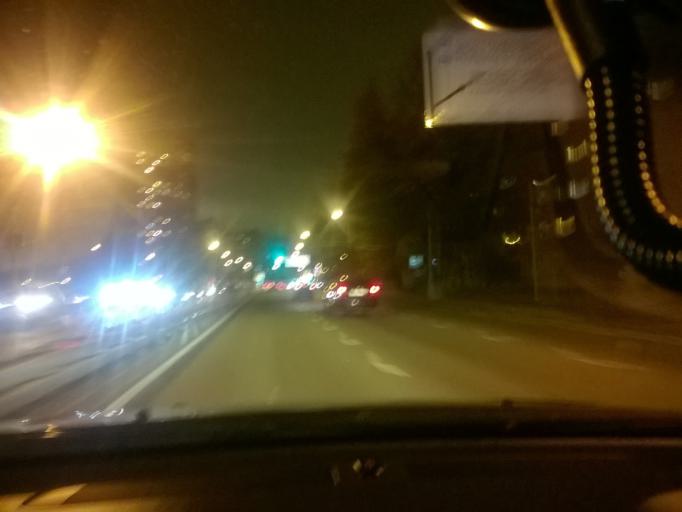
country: RU
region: Moskovskaya
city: Koptevo
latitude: 55.8272
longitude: 37.5300
